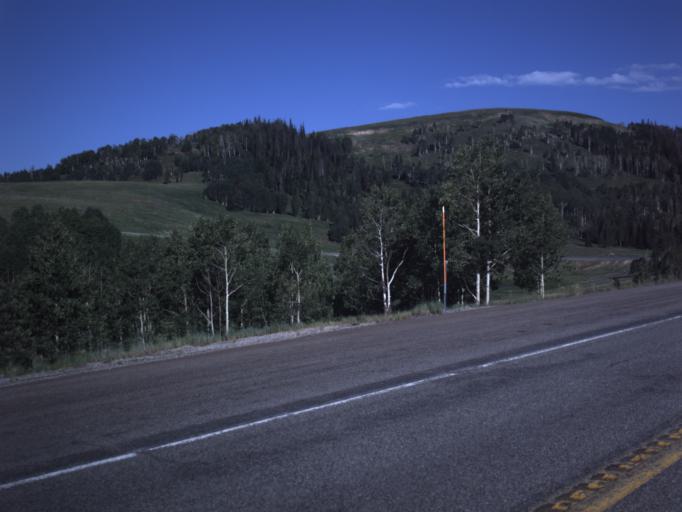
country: US
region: Utah
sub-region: Sanpete County
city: Fairview
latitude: 39.5846
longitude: -111.2370
